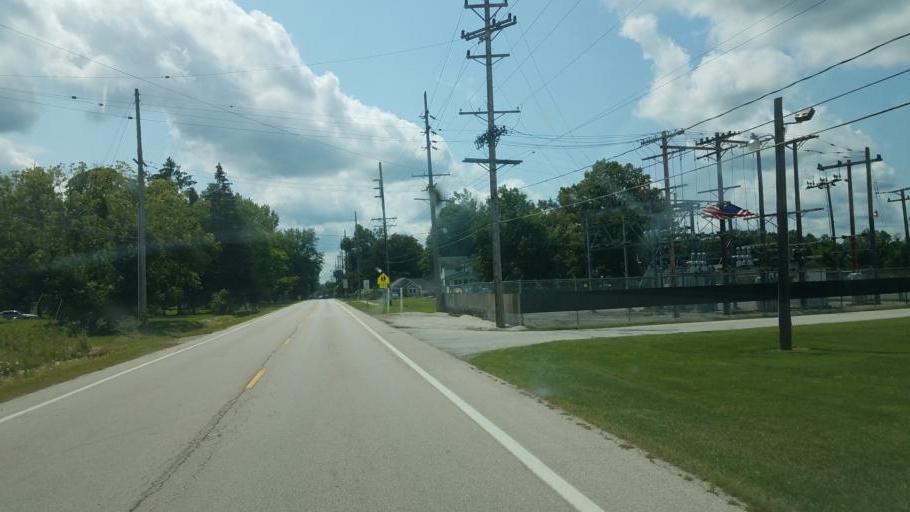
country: US
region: Ohio
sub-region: Ashtabula County
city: Roaming Shores
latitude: 41.6670
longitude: -80.8585
